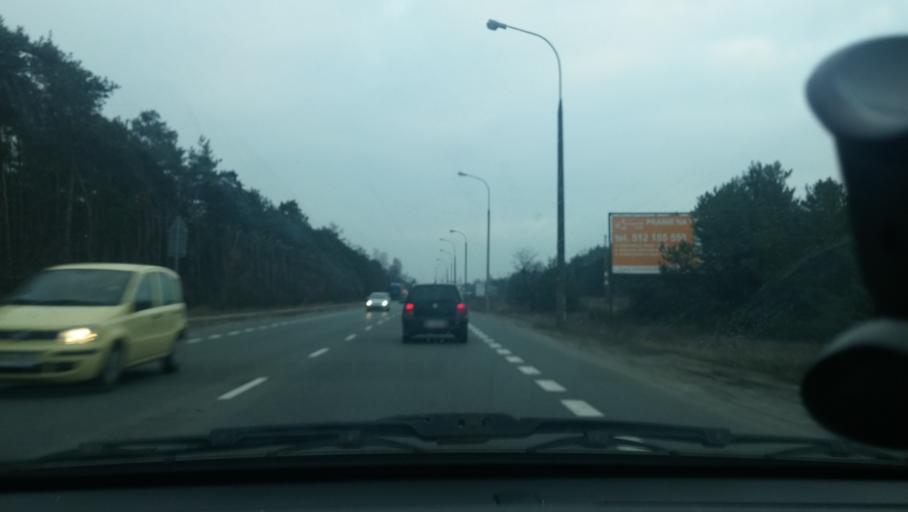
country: PL
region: Masovian Voivodeship
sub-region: Warszawa
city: Wawer
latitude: 52.1972
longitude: 21.1762
